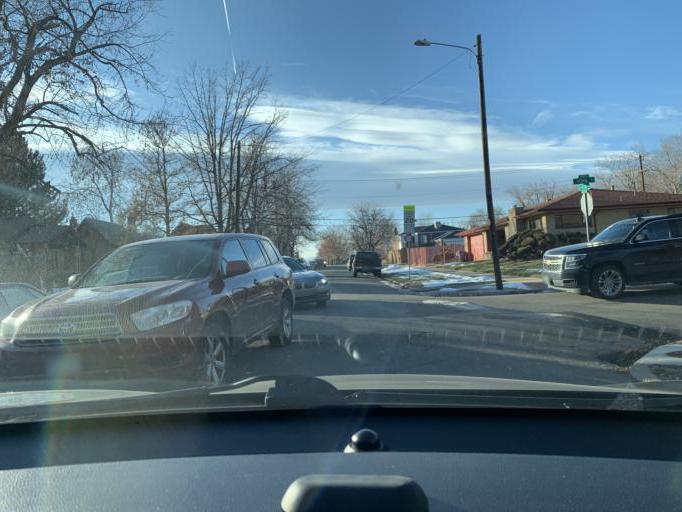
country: US
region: Colorado
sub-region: Adams County
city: Berkley
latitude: 39.7731
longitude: -105.0333
